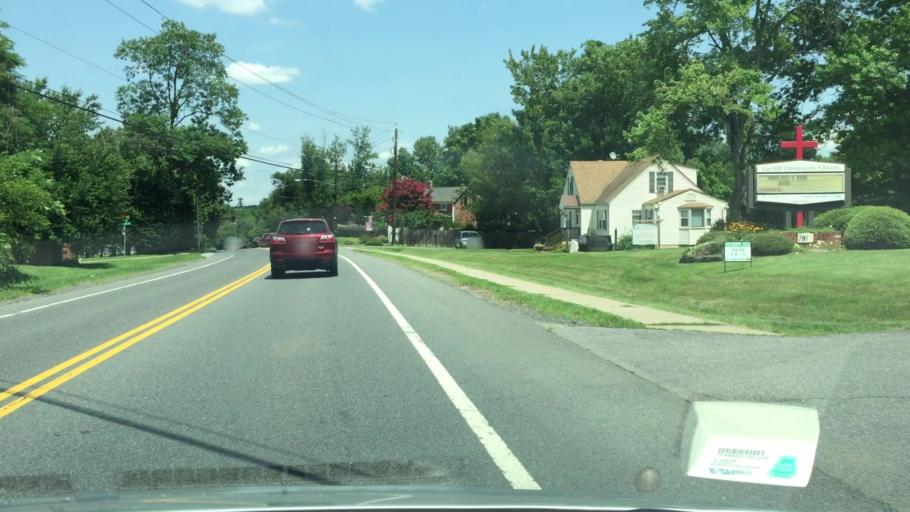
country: US
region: Maryland
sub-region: Montgomery County
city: Layhill
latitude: 39.0914
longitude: -77.0427
